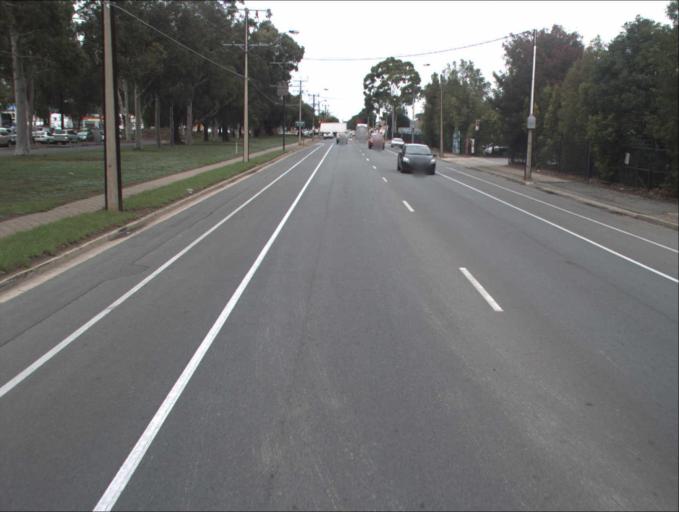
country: AU
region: South Australia
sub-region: Charles Sturt
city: Woodville
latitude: -34.8732
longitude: 138.5662
